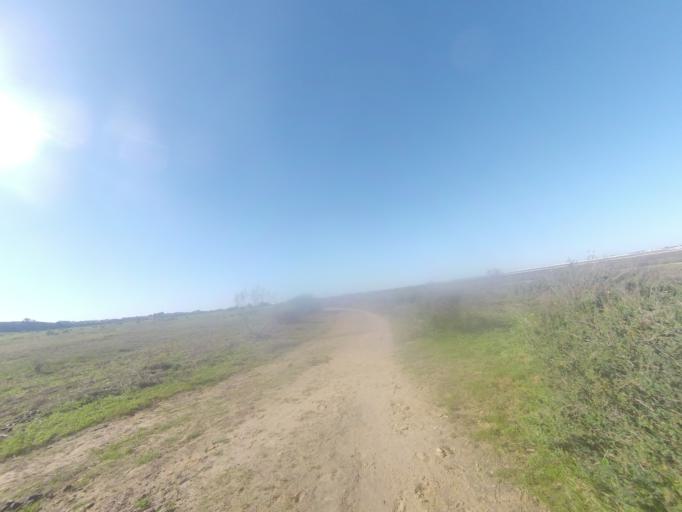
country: ES
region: Andalusia
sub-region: Provincia de Huelva
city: Palos de la Frontera
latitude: 37.2407
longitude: -6.8903
